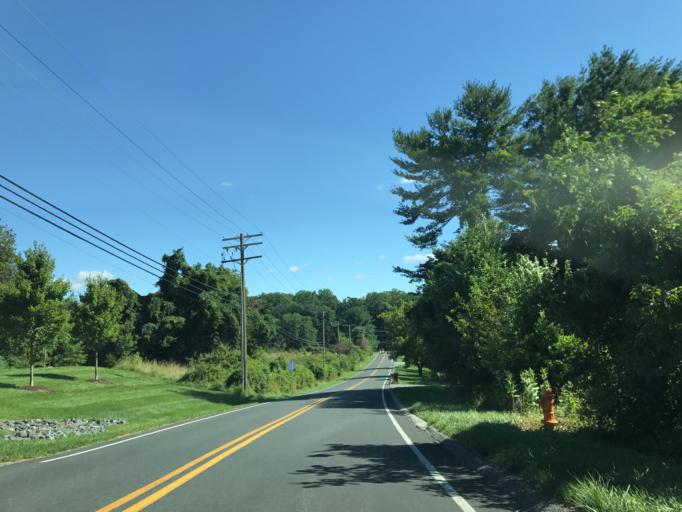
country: US
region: Maryland
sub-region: Howard County
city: Ilchester
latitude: 39.2406
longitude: -76.7687
